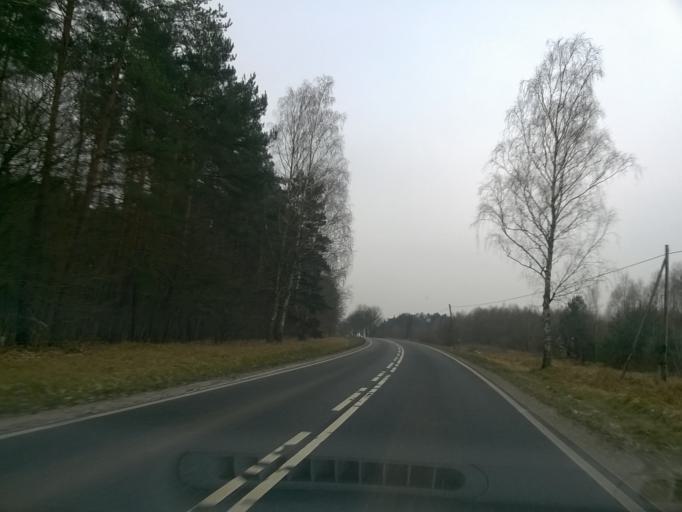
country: PL
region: Kujawsko-Pomorskie
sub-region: Powiat nakielski
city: Kcynia
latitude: 53.0385
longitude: 17.5453
